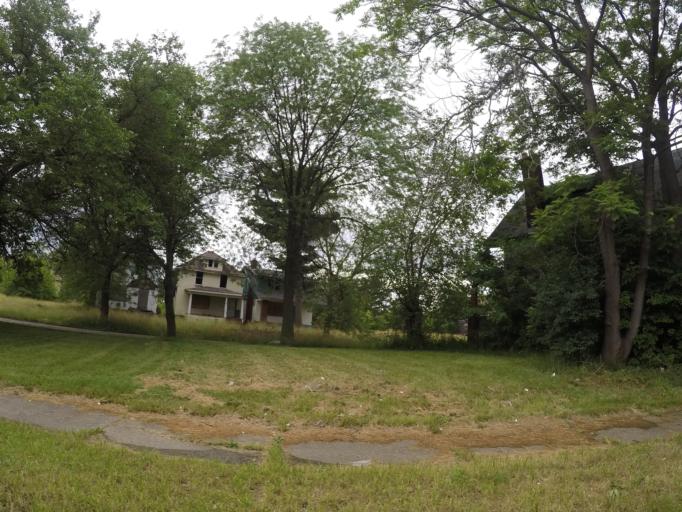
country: US
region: Michigan
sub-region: Wayne County
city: Highland Park
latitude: 42.4176
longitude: -83.1118
